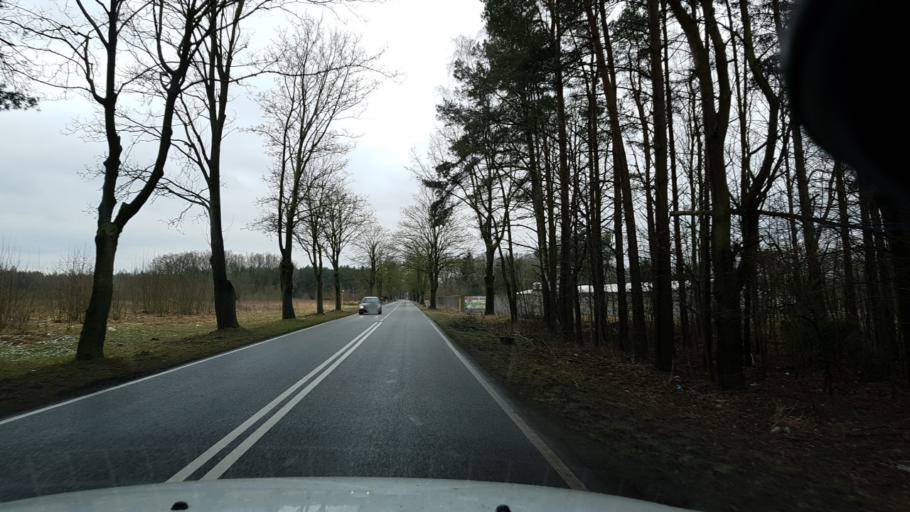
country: PL
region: West Pomeranian Voivodeship
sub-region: Powiat goleniowski
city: Goleniow
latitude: 53.6111
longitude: 14.7411
